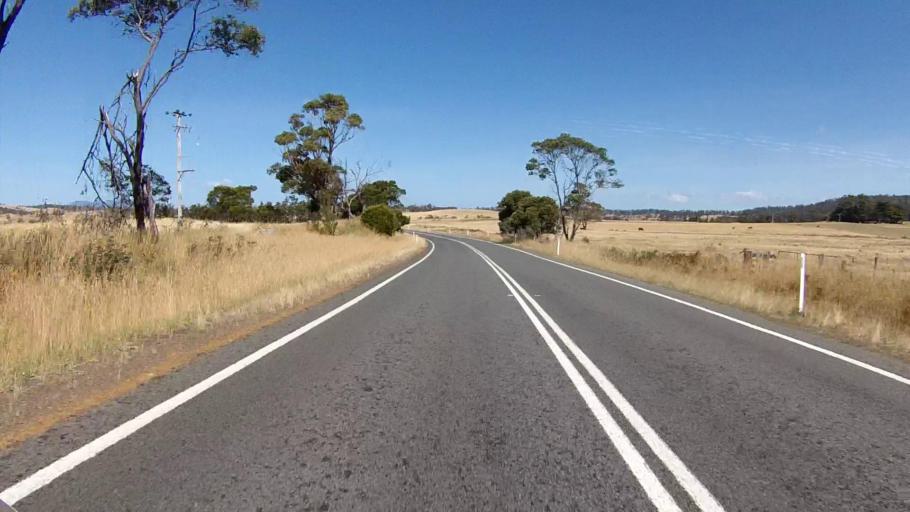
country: AU
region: Tasmania
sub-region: Sorell
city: Sorell
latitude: -42.4475
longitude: 147.9291
